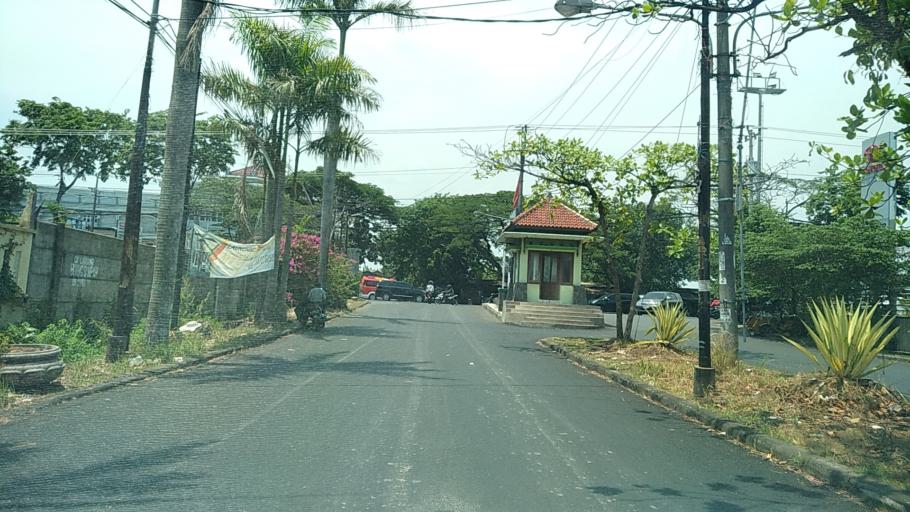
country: ID
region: Central Java
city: Mranggen
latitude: -7.0141
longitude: 110.4820
